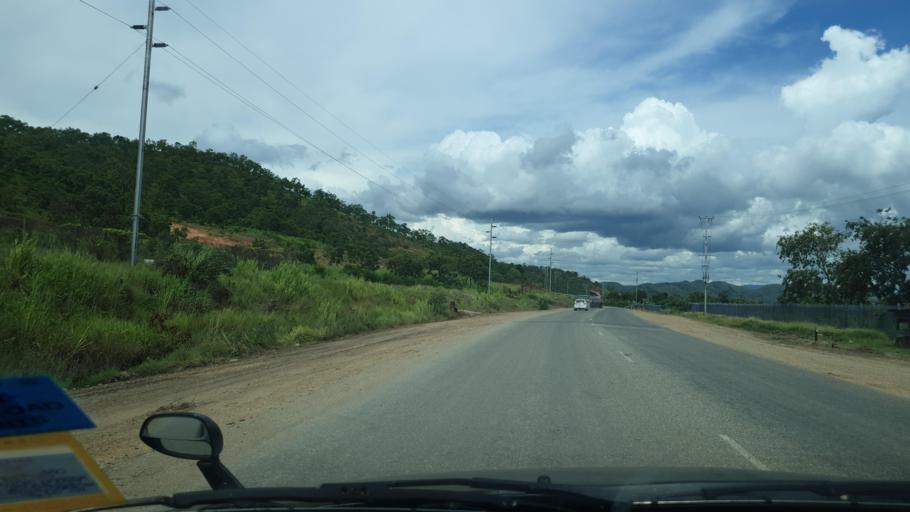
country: PG
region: National Capital
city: Port Moresby
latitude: -9.4195
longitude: 147.0839
